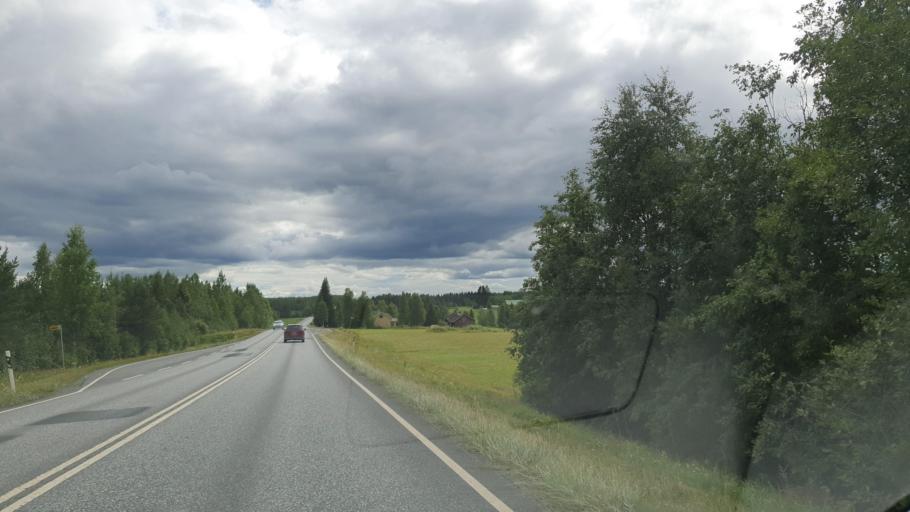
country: FI
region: Northern Savo
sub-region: Ylae-Savo
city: Sonkajaervi
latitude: 63.8210
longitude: 27.4209
